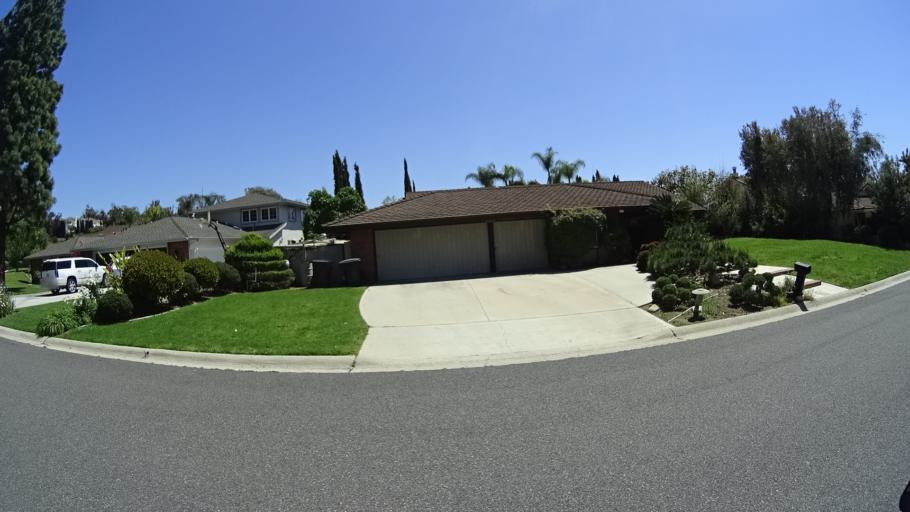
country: US
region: California
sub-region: Orange County
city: Villa Park
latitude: 33.8244
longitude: -117.8071
